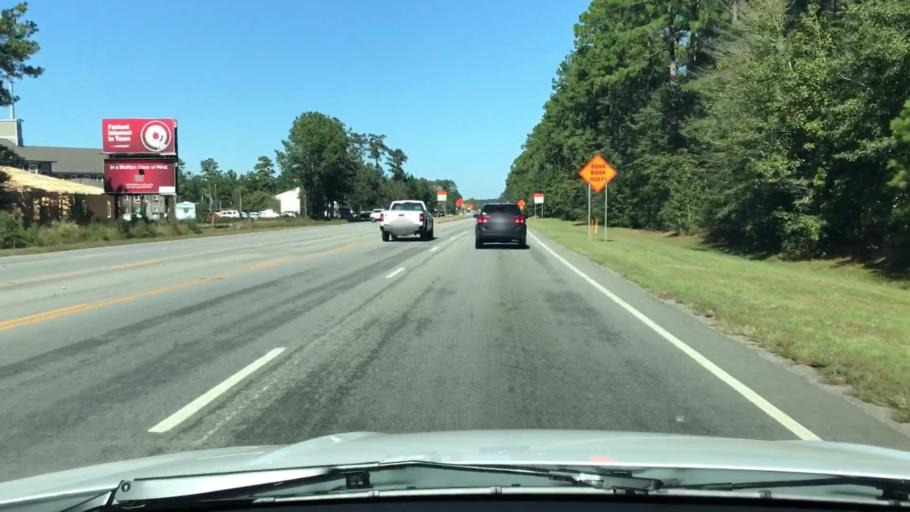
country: US
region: South Carolina
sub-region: Beaufort County
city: Bluffton
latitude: 32.3069
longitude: -80.9349
